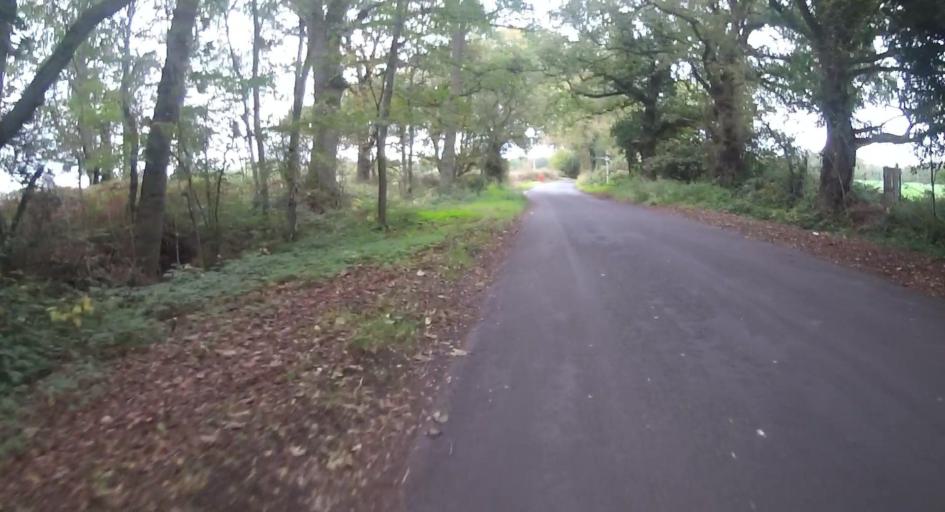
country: GB
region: England
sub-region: Hampshire
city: Fleet
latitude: 51.2822
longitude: -0.8805
